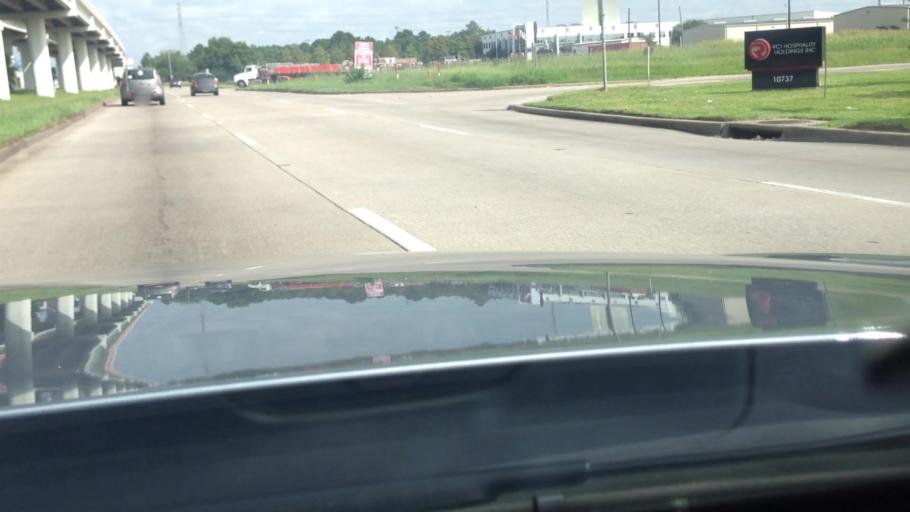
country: US
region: Texas
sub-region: Harris County
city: Hudson
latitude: 29.9385
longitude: -95.5176
